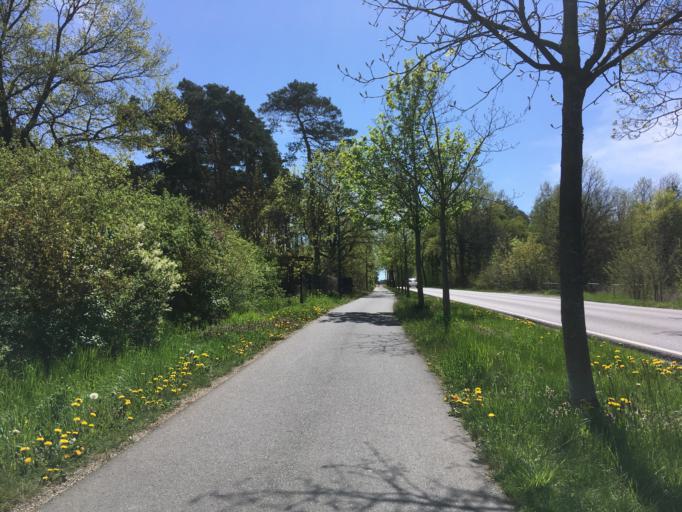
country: DE
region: Brandenburg
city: Wildau
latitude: 52.3270
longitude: 13.6126
